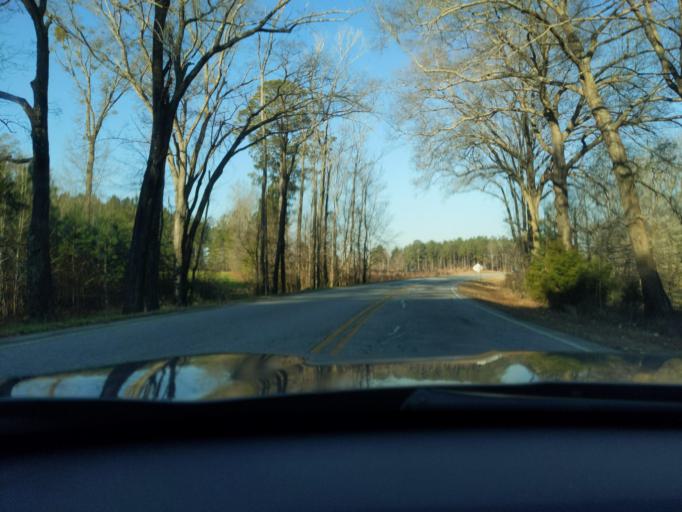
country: US
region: South Carolina
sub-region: Newberry County
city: Newberry
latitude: 34.2106
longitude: -81.7018
